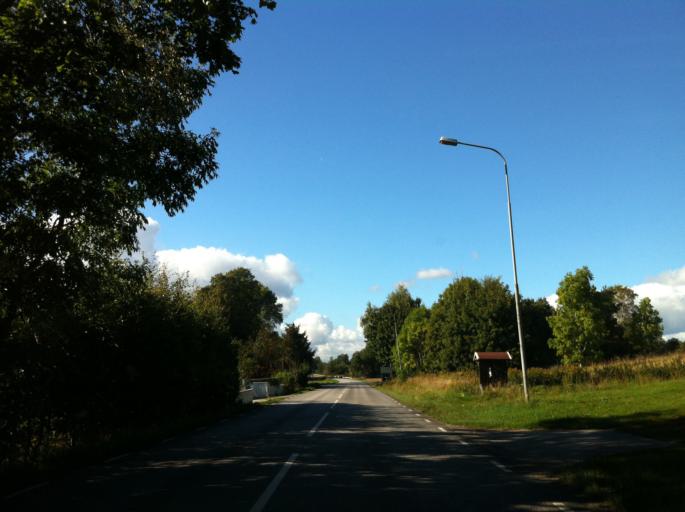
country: SE
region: Skane
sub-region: Hoors Kommun
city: Loberod
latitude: 55.7388
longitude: 13.4364
